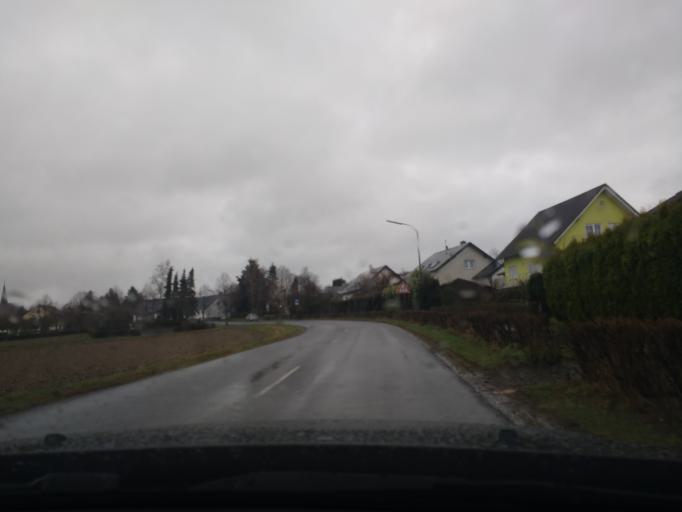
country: DE
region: Rheinland-Pfalz
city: Irmenach
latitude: 49.9201
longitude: 7.1887
